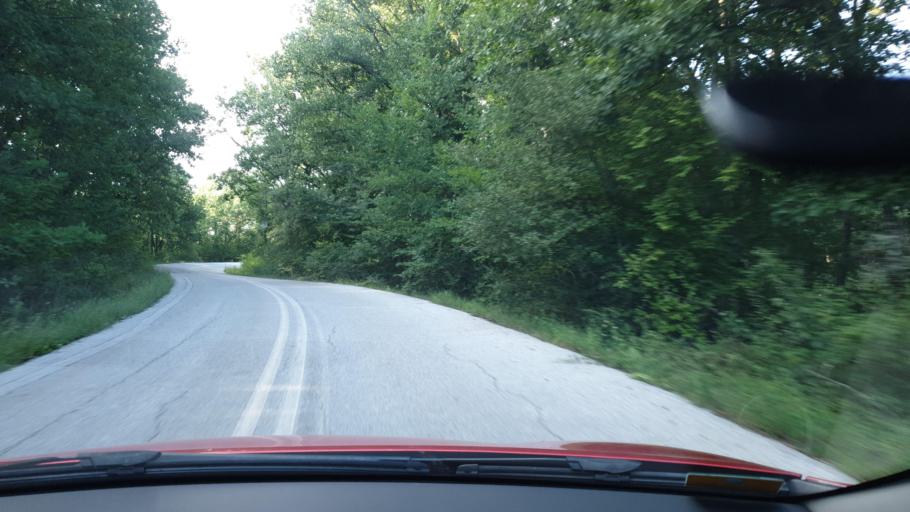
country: GR
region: Central Macedonia
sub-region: Nomos Chalkidikis
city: Galatista
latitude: 40.5374
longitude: 23.2780
